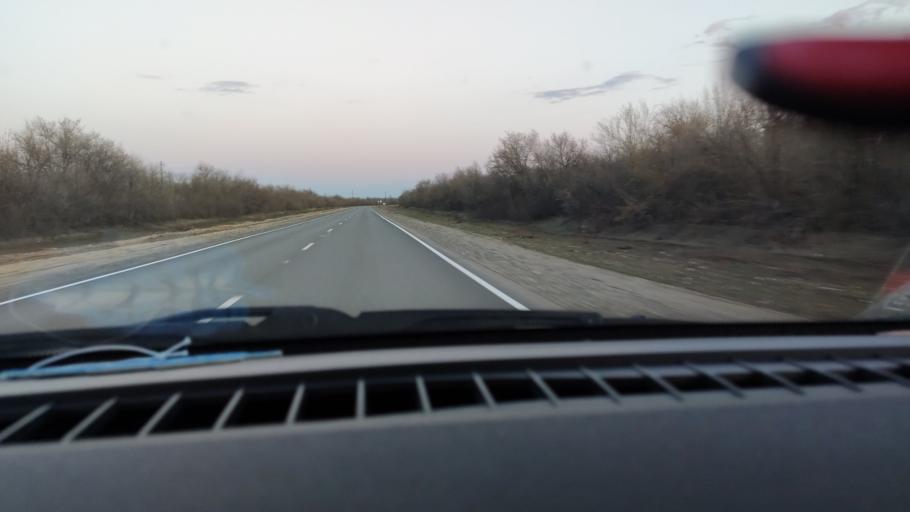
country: RU
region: Saratov
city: Privolzhskiy
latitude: 51.1584
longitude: 45.9600
